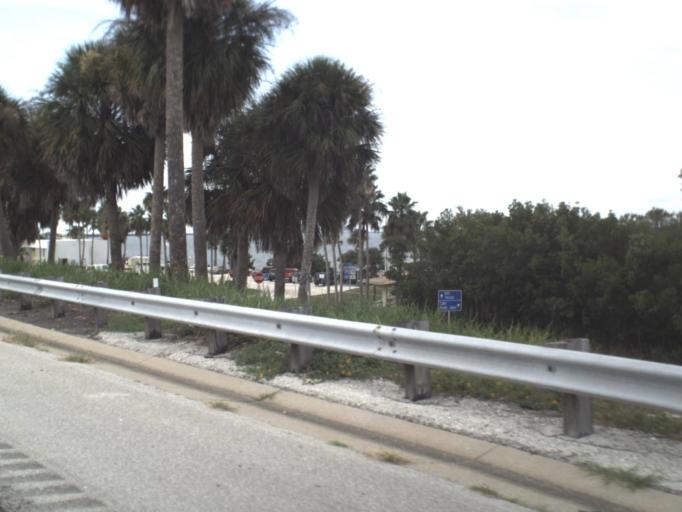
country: US
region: Florida
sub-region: Manatee County
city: Memphis
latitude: 27.5838
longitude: -82.6124
